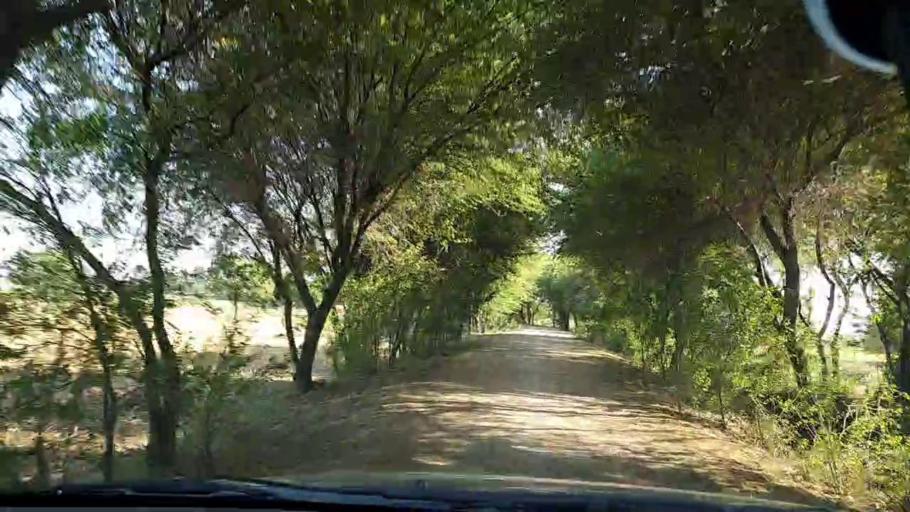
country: PK
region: Sindh
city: Mirpur Batoro
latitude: 24.6300
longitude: 68.2654
